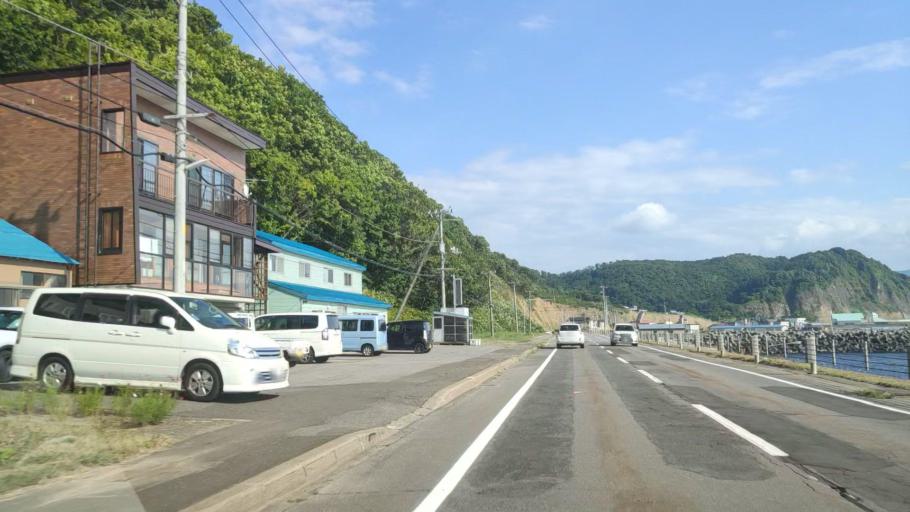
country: JP
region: Hokkaido
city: Ishikari
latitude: 43.6078
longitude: 141.3799
